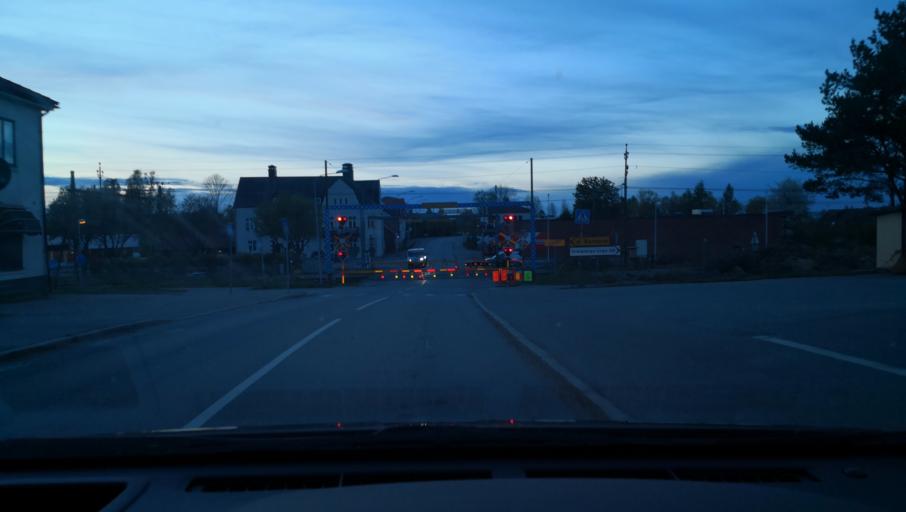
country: SE
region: OErebro
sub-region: Askersunds Kommun
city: Askersund
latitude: 59.0223
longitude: 14.8699
